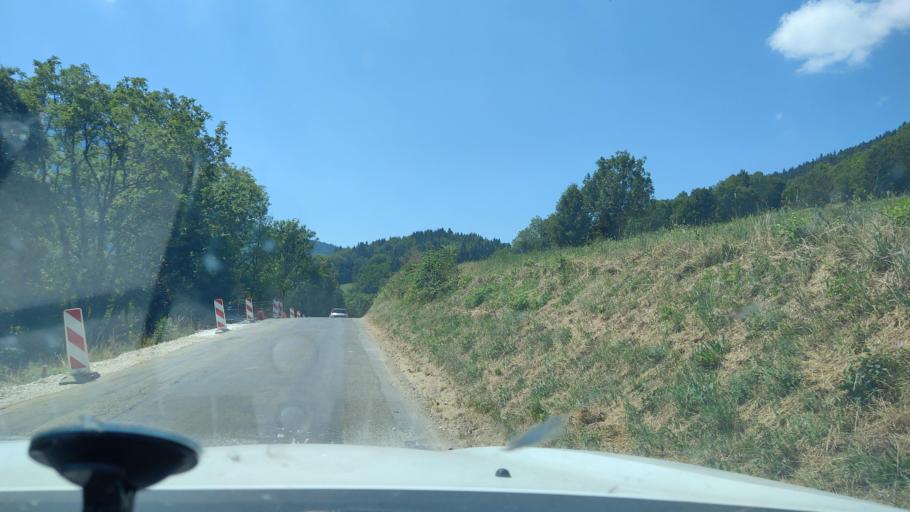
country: FR
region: Rhone-Alpes
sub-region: Departement de la Savoie
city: Mery
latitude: 45.6652
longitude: 6.0346
